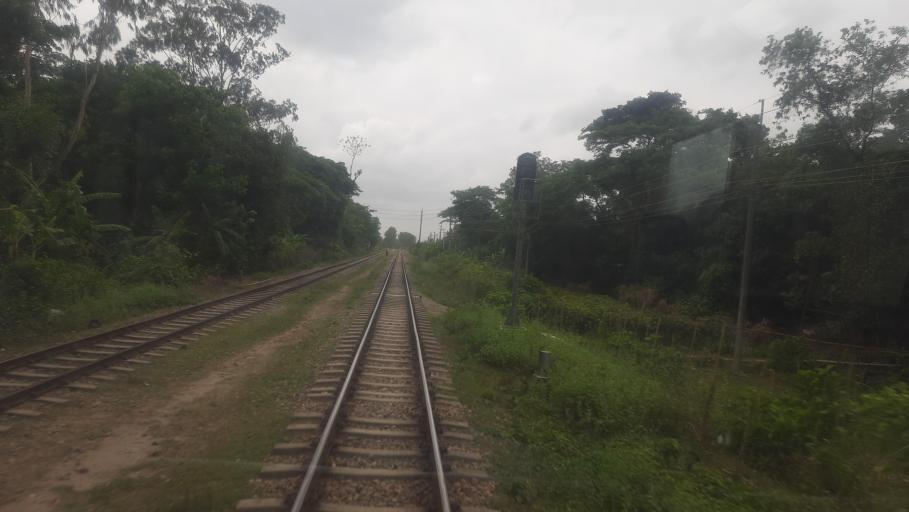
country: BD
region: Chittagong
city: Fatikchari
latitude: 22.7643
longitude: 91.5931
